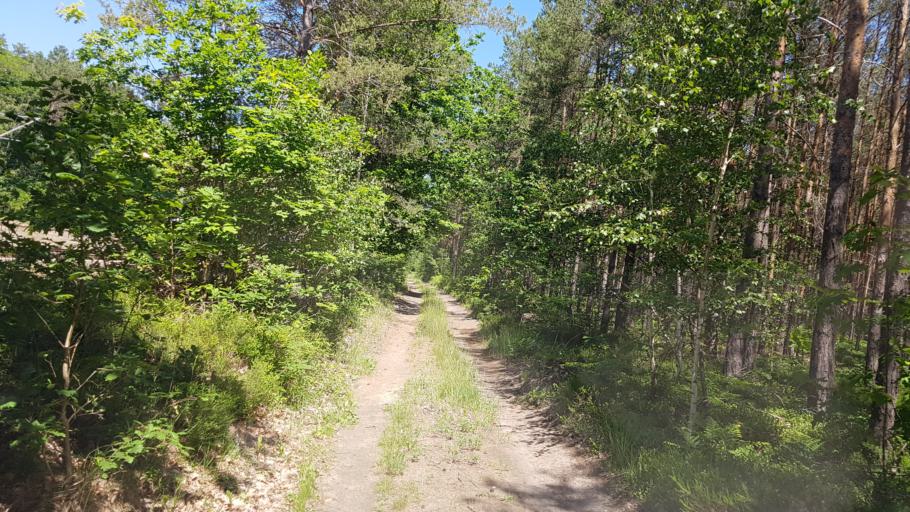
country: DE
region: Brandenburg
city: Ruckersdorf
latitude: 51.5390
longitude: 13.5765
